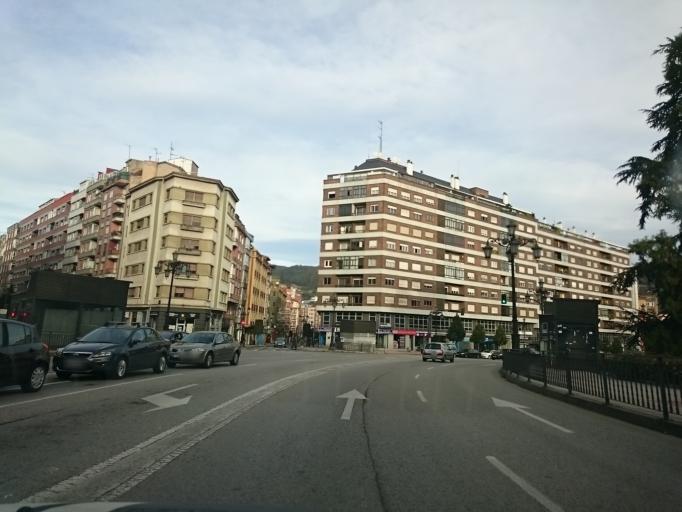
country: ES
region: Asturias
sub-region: Province of Asturias
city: Oviedo
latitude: 43.3634
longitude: -5.8600
